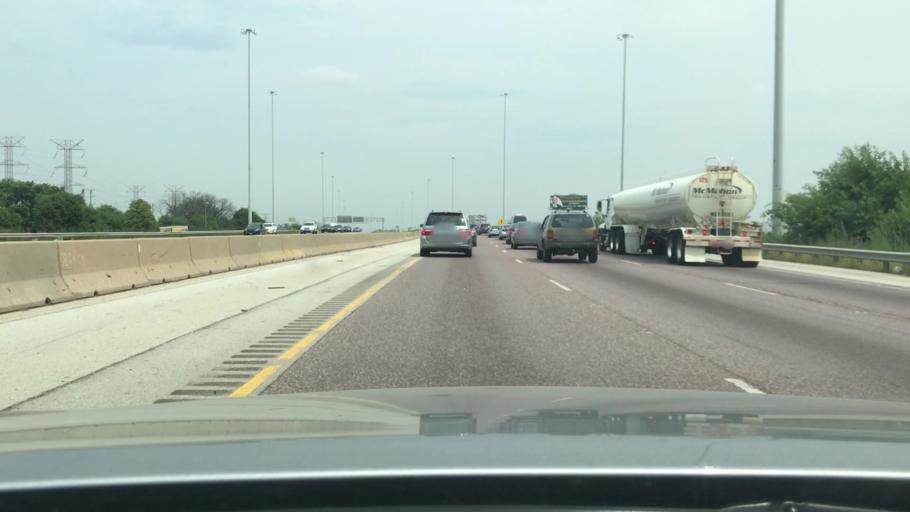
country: US
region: Illinois
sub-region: Cook County
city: Cicero
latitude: 41.8176
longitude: -87.7420
